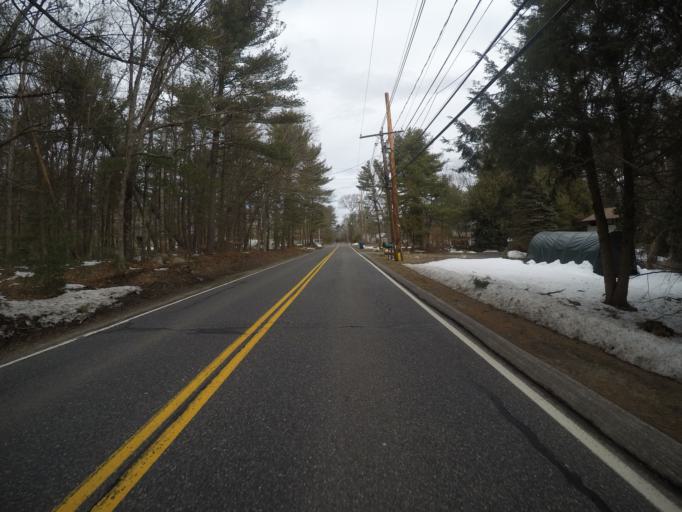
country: US
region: Massachusetts
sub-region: Bristol County
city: Easton
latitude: 42.0588
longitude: -71.1316
